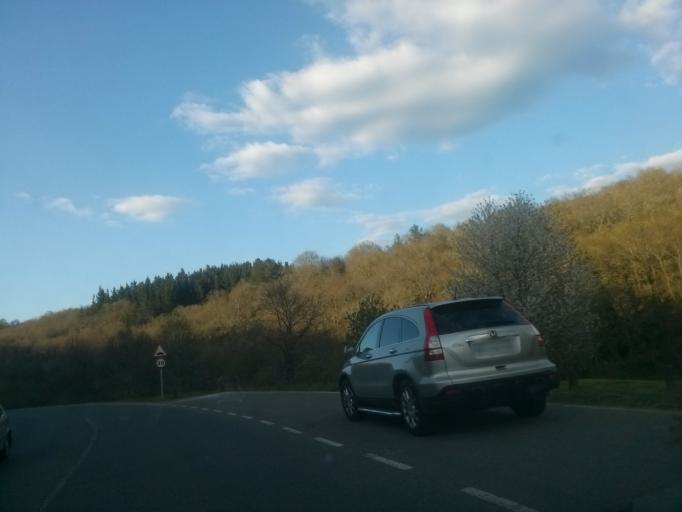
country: ES
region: Galicia
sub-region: Provincia de Lugo
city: Lugo
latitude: 42.9979
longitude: -7.5313
